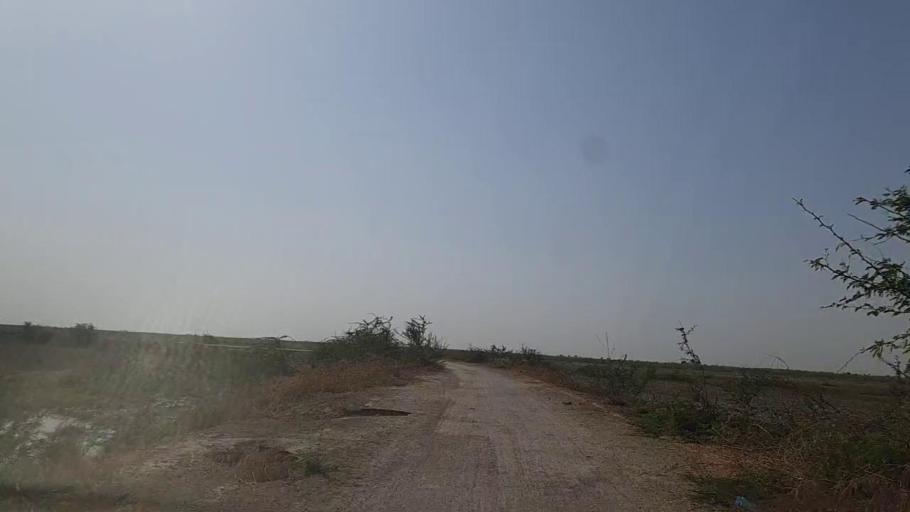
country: PK
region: Sindh
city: Naukot
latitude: 24.5950
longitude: 69.3096
